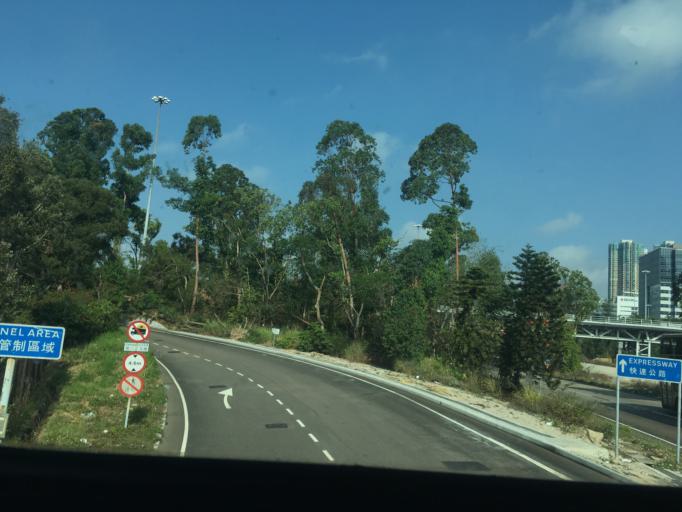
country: HK
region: Kowloon City
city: Kowloon
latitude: 22.3092
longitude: 114.1635
